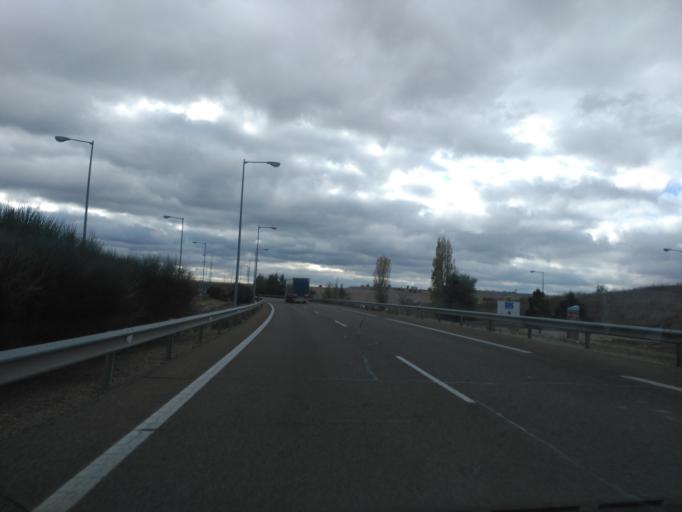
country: ES
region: Castille and Leon
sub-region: Provincia de Valladolid
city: Zaratan
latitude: 41.6560
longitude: -4.7640
